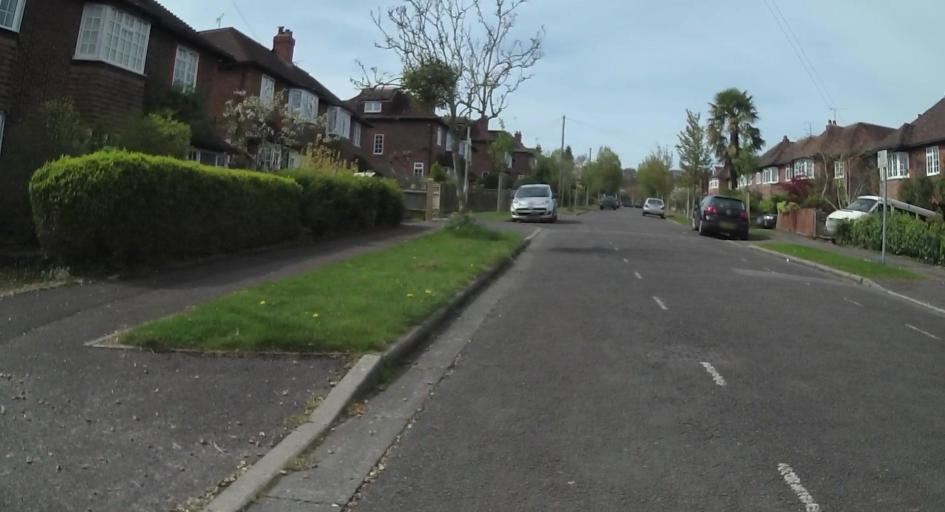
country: GB
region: England
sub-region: Hampshire
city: Winchester
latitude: 51.0667
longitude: -1.3292
